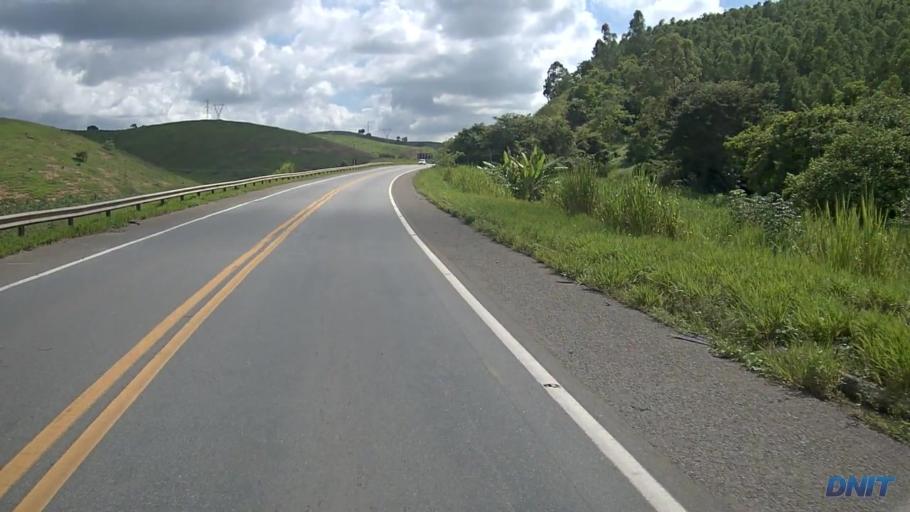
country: BR
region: Minas Gerais
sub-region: Belo Oriente
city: Belo Oriente
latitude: -19.1050
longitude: -42.2018
